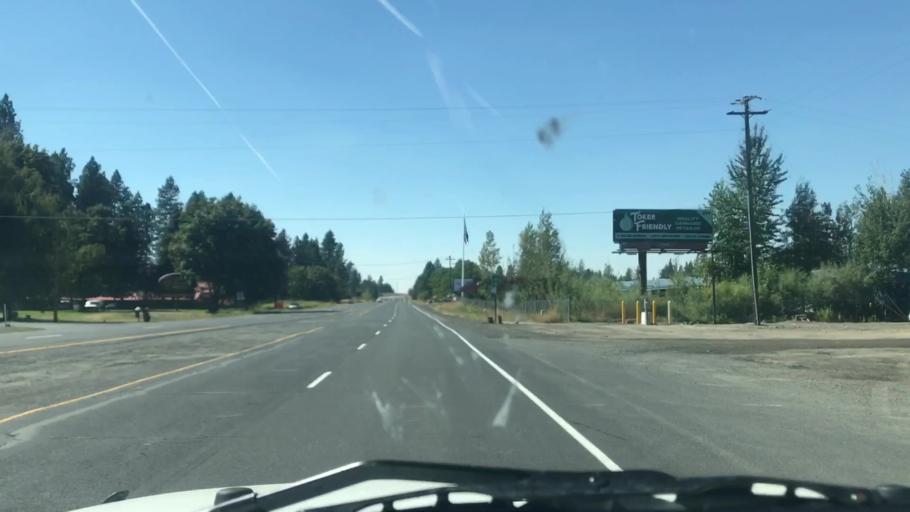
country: US
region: Washington
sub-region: Spokane County
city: Spokane
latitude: 47.6431
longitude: -117.4884
